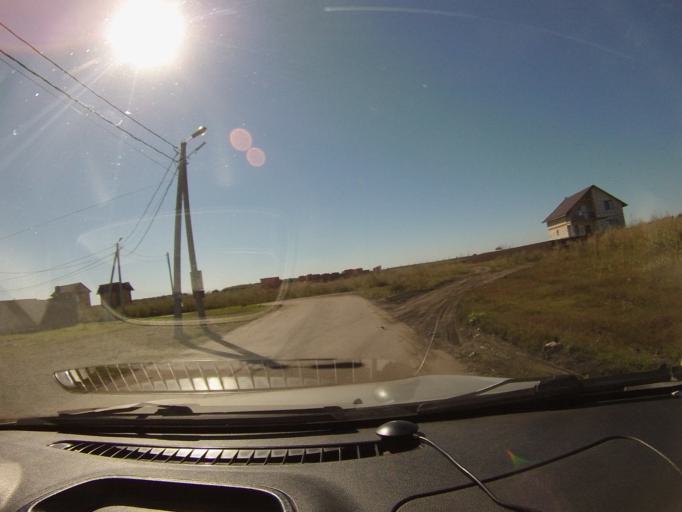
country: RU
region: Tambov
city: Komsomolets
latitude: 52.7734
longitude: 41.3586
